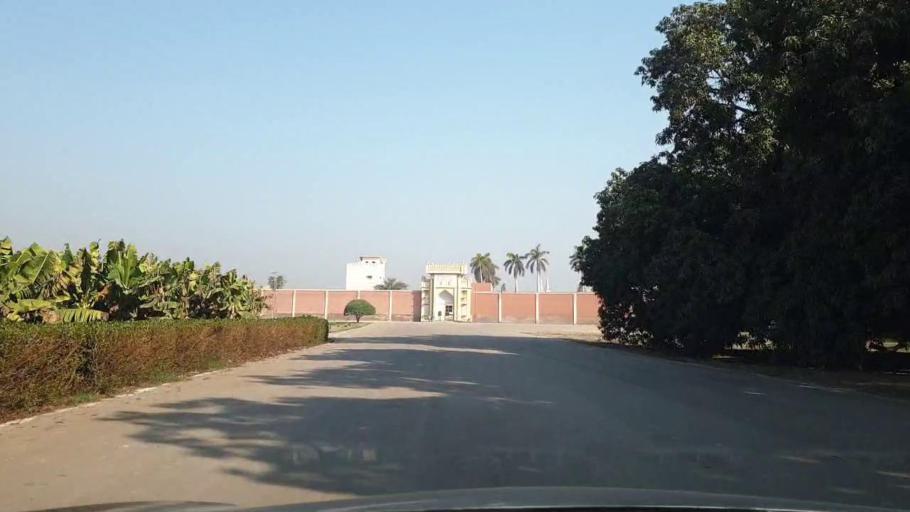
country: PK
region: Sindh
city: Tando Allahyar
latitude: 25.5103
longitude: 68.7208
